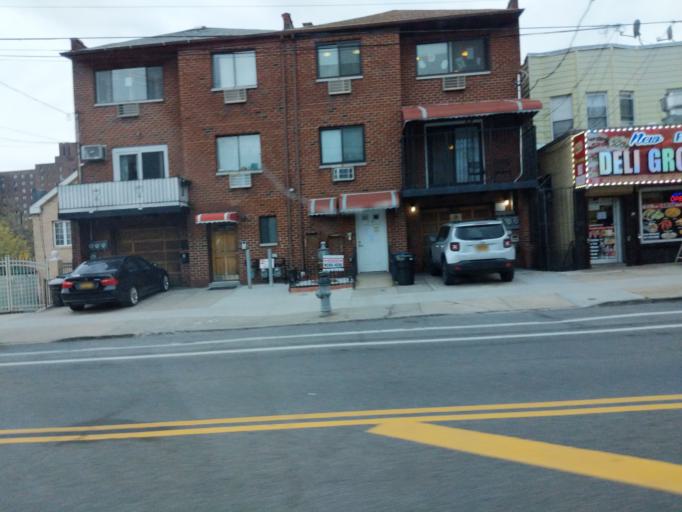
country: US
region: New York
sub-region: Bronx
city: The Bronx
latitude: 40.8402
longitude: -73.8529
